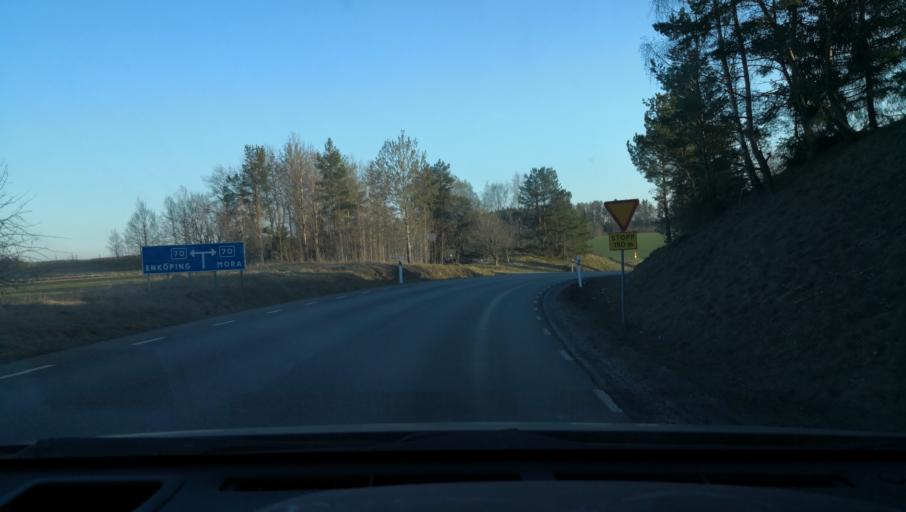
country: SE
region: Uppsala
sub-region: Enkopings Kommun
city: Irsta
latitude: 59.7712
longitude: 16.9133
